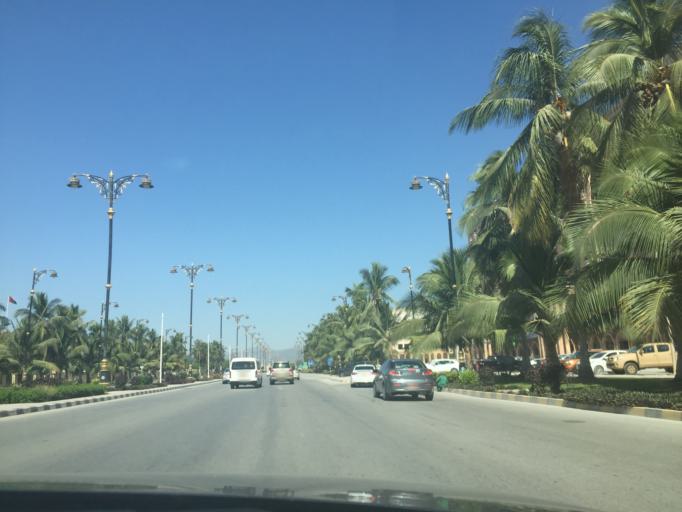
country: OM
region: Zufar
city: Salalah
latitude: 17.0203
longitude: 54.0920
